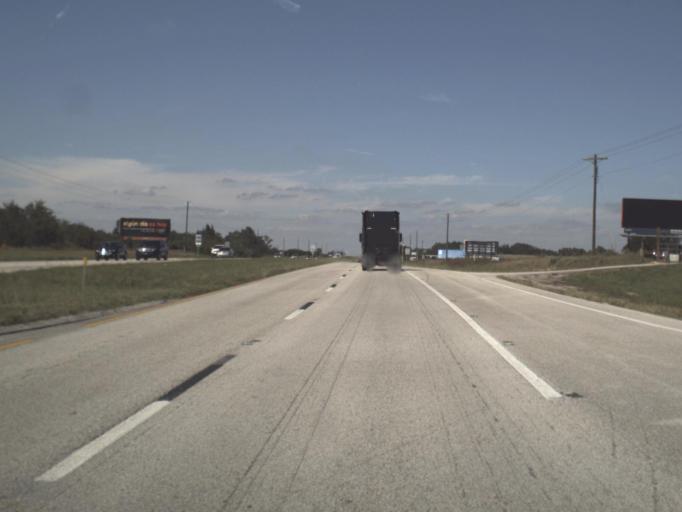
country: US
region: Florida
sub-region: Highlands County
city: Sebring
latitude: 27.4131
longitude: -81.4164
